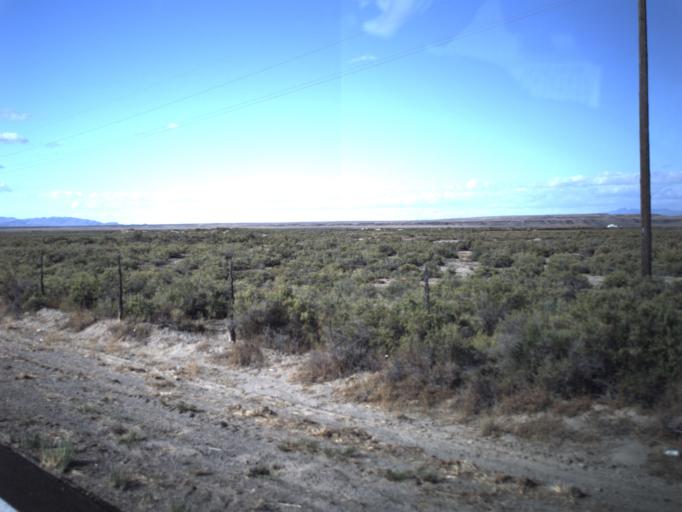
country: US
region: Utah
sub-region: Millard County
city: Delta
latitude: 39.2389
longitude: -112.6639
